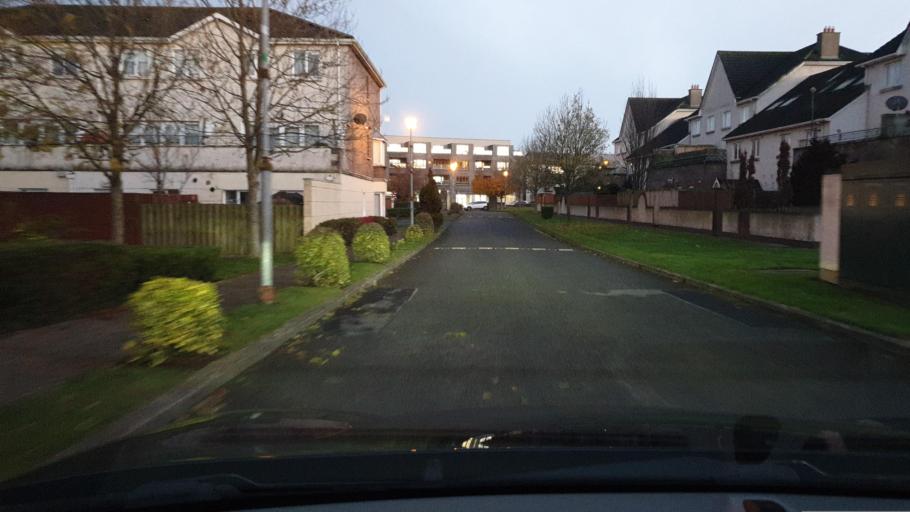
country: IE
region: Leinster
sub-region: An Mhi
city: Ashbourne
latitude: 53.5148
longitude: -6.4054
